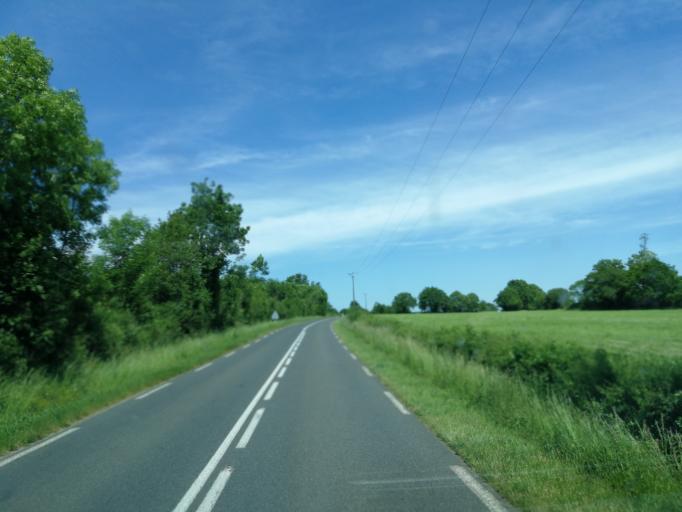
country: FR
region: Poitou-Charentes
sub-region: Departement des Deux-Sevres
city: Bressuire
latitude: 46.8195
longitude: -0.5279
